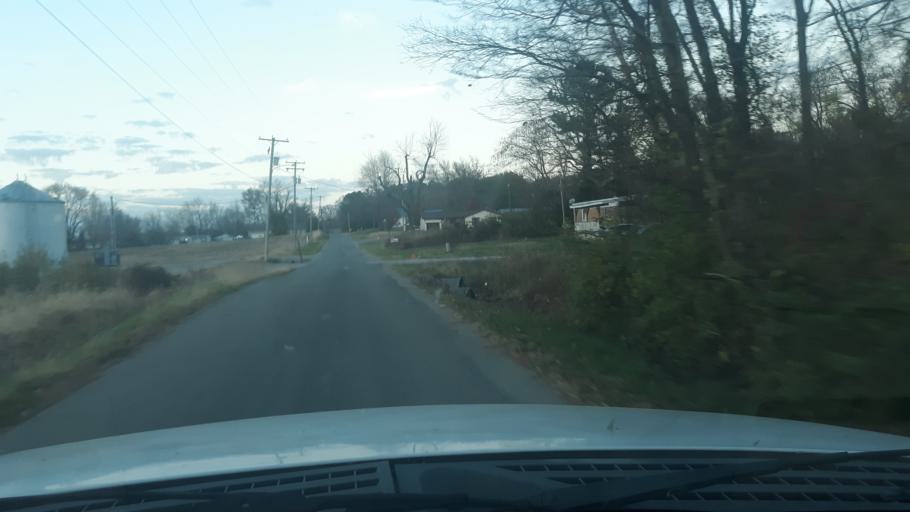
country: US
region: Illinois
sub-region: Saline County
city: Harrisburg
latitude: 37.8464
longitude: -88.6145
